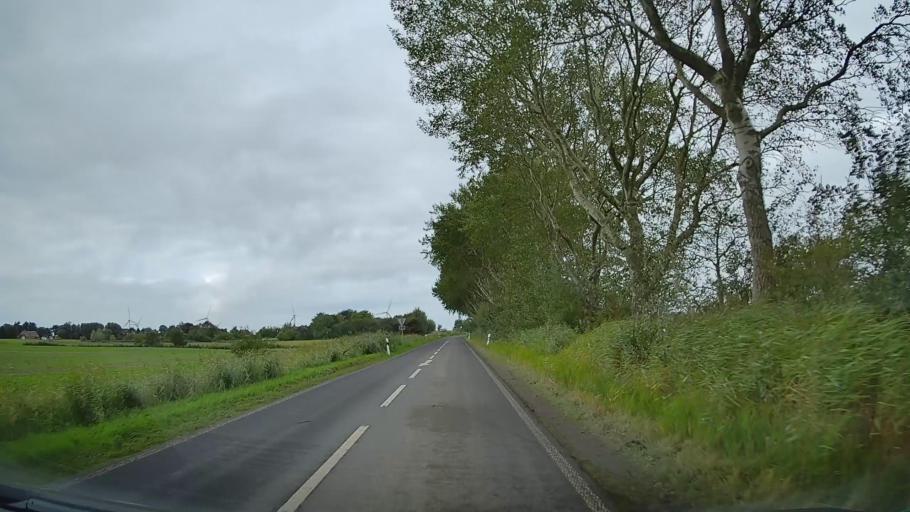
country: DE
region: Schleswig-Holstein
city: Friedrich-Wilhelm-Lubke-Koog
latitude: 54.8355
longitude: 8.6608
